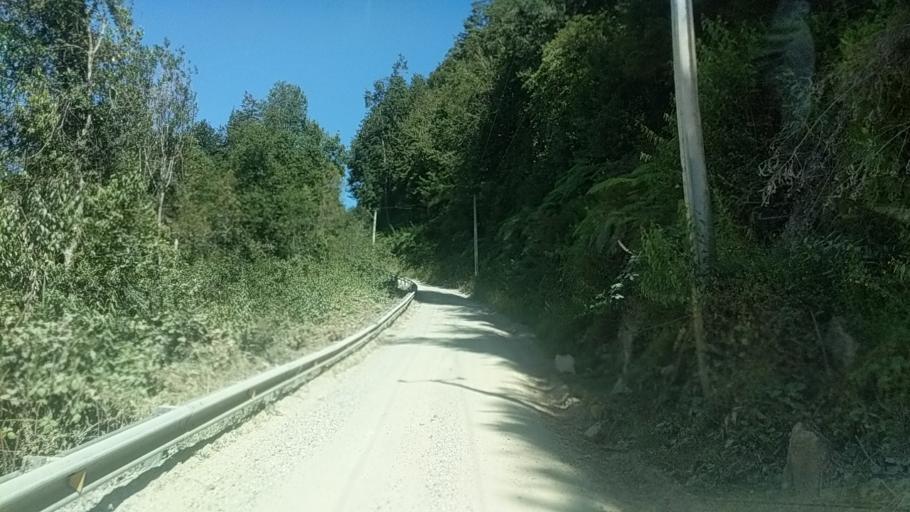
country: CL
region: Araucania
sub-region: Provincia de Cautin
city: Pucon
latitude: -39.0634
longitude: -71.7262
